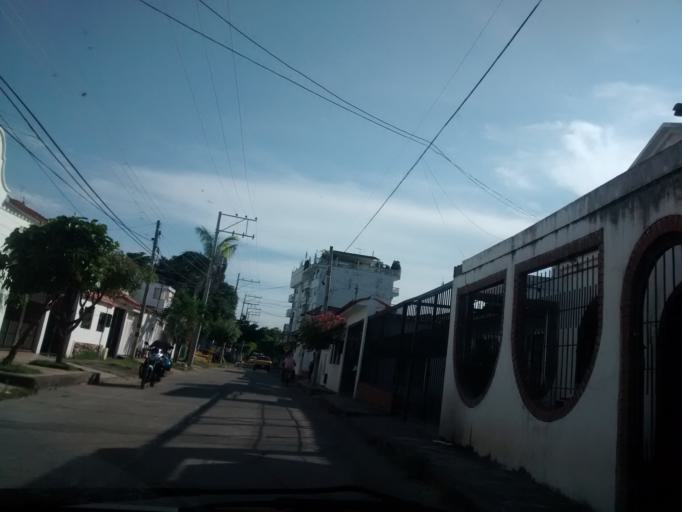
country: CO
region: Cundinamarca
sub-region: Girardot
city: Girardot City
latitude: 4.3071
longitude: -74.7999
